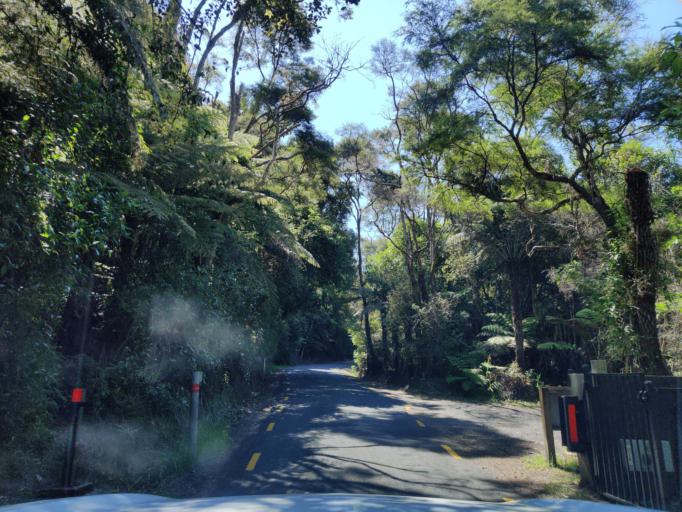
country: NZ
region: Auckland
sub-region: Auckland
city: Red Hill
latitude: -37.0657
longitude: 175.0883
